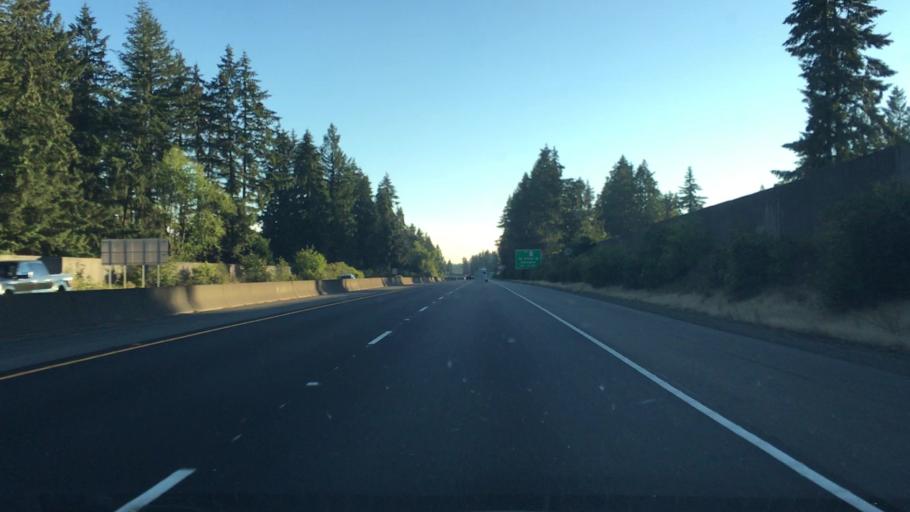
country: US
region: Washington
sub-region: King County
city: Covington
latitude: 47.3662
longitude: -122.1061
